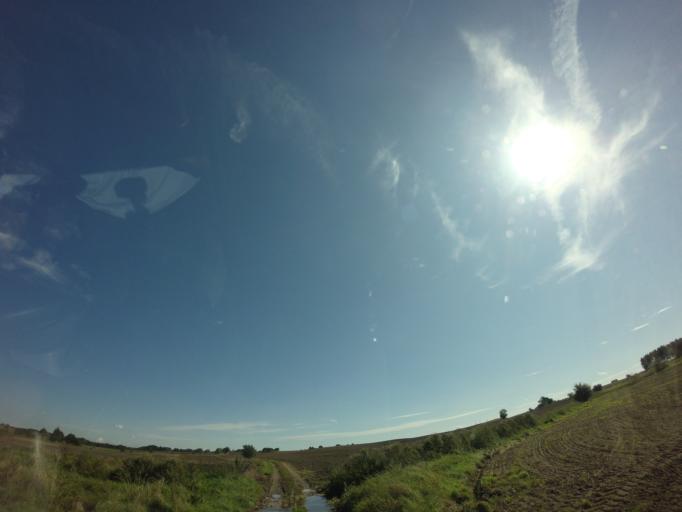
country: PL
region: West Pomeranian Voivodeship
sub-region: Powiat choszczenski
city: Recz
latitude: 53.2519
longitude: 15.5627
